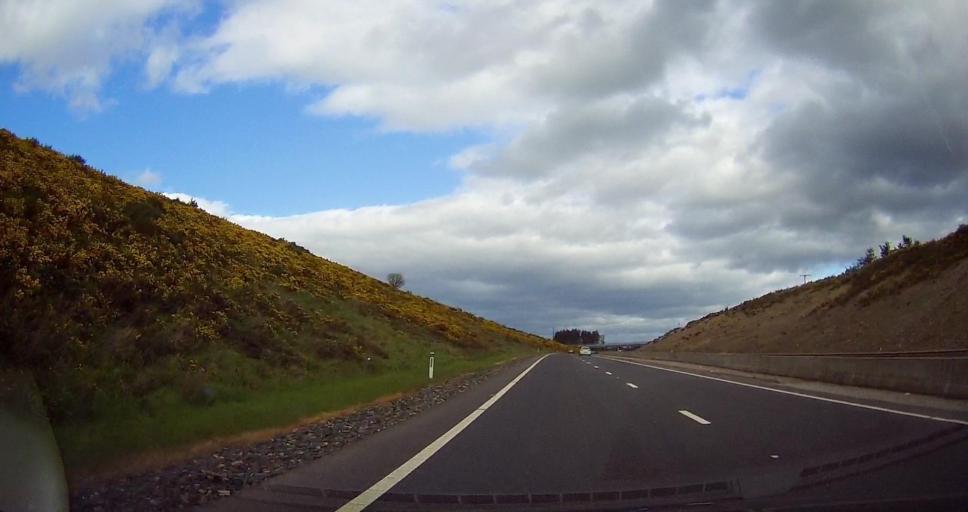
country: GB
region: Scotland
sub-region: Aberdeen City
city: Cults
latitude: 57.0786
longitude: -2.1925
